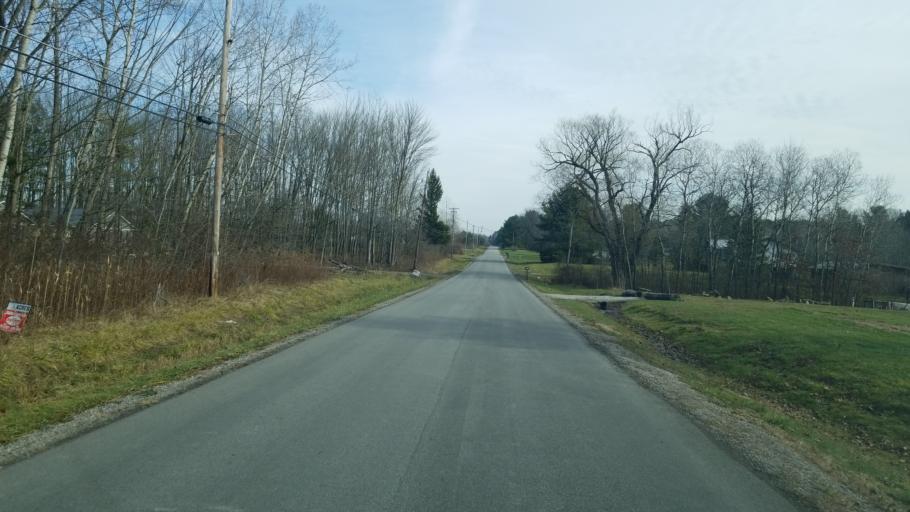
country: US
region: Ohio
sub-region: Ashtabula County
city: Roaming Shores
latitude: 41.6546
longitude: -80.8276
